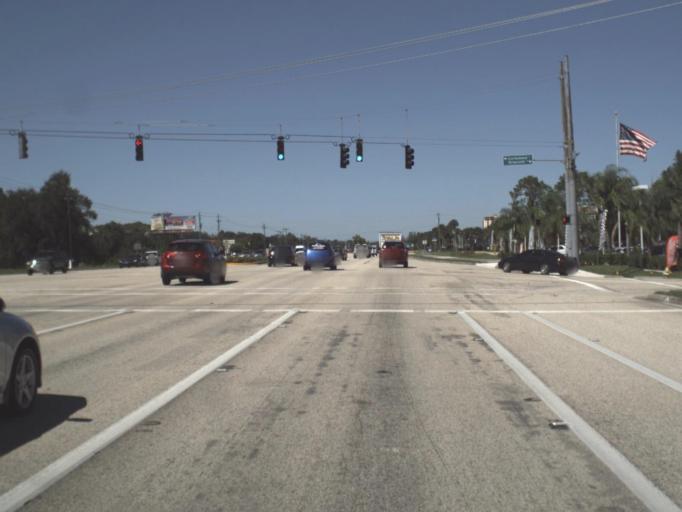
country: US
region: Florida
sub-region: Lee County
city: Villas
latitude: 26.5150
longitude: -81.8647
